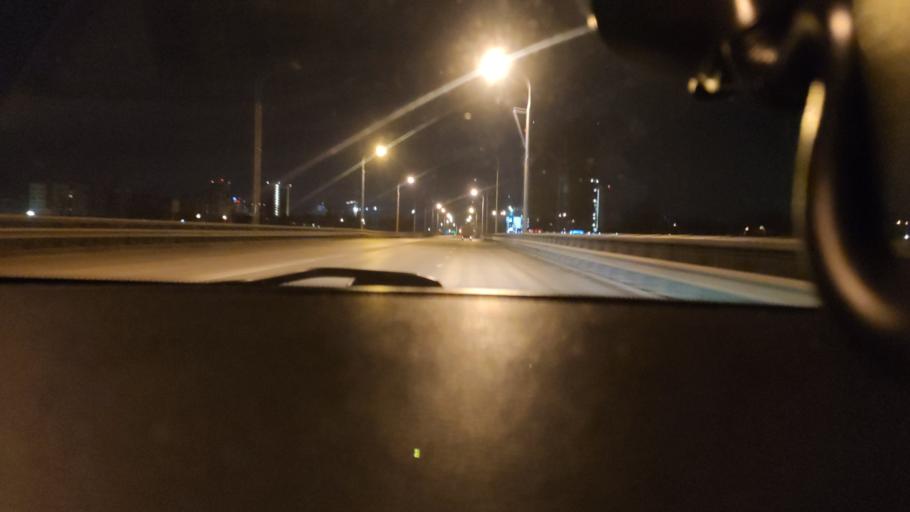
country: RU
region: Perm
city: Perm
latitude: 58.0203
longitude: 56.2220
